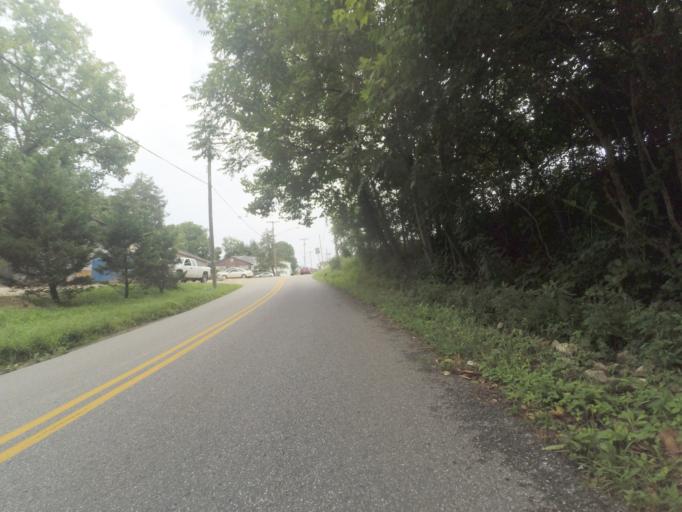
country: US
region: West Virginia
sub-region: Cabell County
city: Huntington
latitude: 38.4033
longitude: -82.3983
